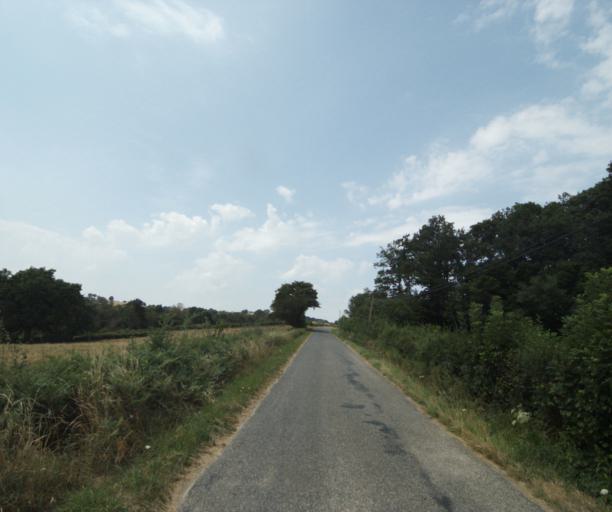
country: FR
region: Bourgogne
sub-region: Departement de Saone-et-Loire
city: Gueugnon
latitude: 46.5994
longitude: 4.0151
